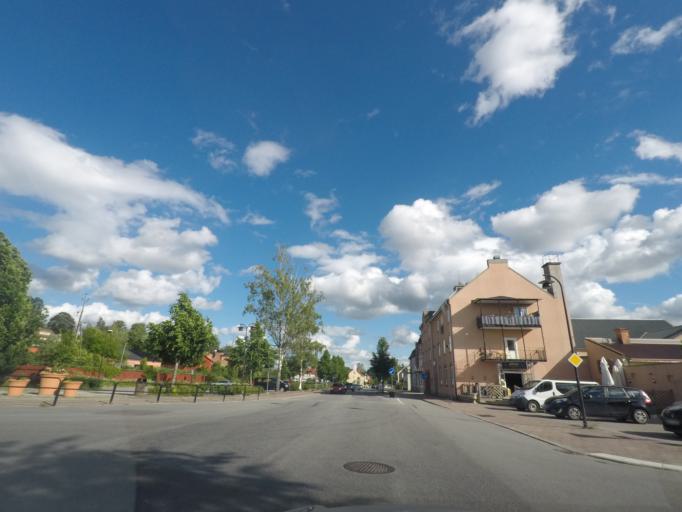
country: SE
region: OErebro
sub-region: Lindesbergs Kommun
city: Lindesberg
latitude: 59.5917
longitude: 15.2299
